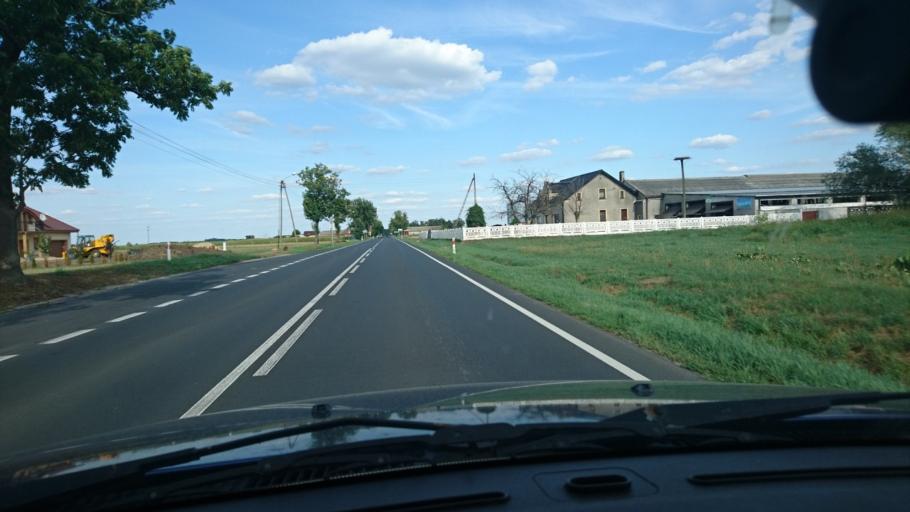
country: PL
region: Greater Poland Voivodeship
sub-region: Powiat krotoszynski
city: Kobylin
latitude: 51.7295
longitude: 17.2747
